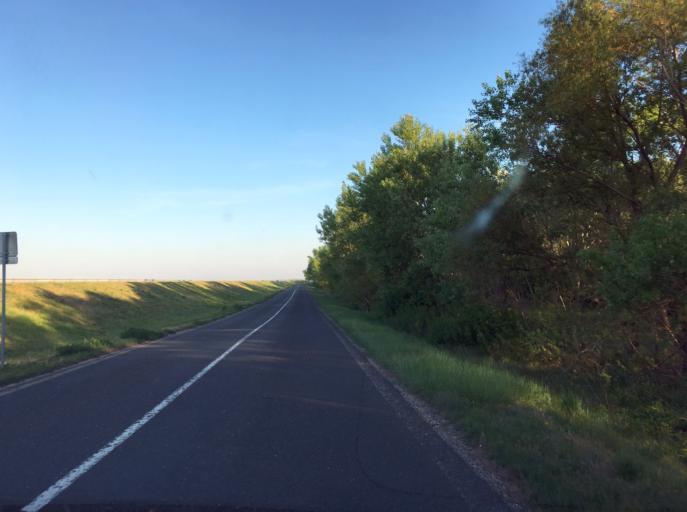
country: HU
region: Gyor-Moson-Sopron
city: Rajka
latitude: 48.0317
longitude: 17.2359
